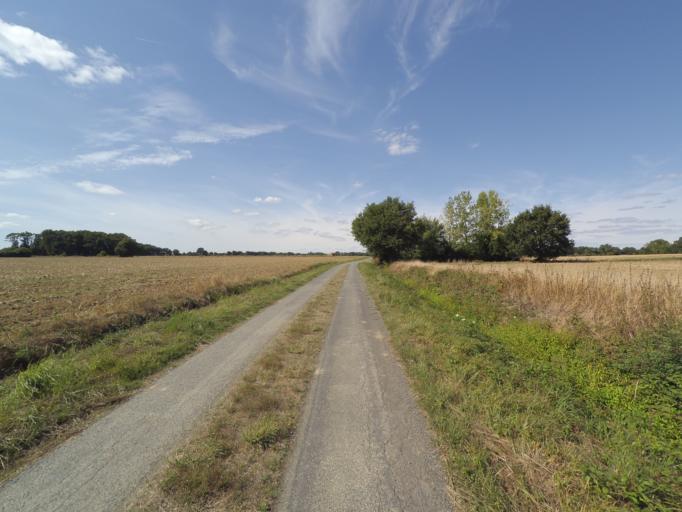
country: FR
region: Pays de la Loire
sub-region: Departement de la Vendee
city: Saint-Andre-Treize-Voies
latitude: 46.9525
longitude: -1.4121
